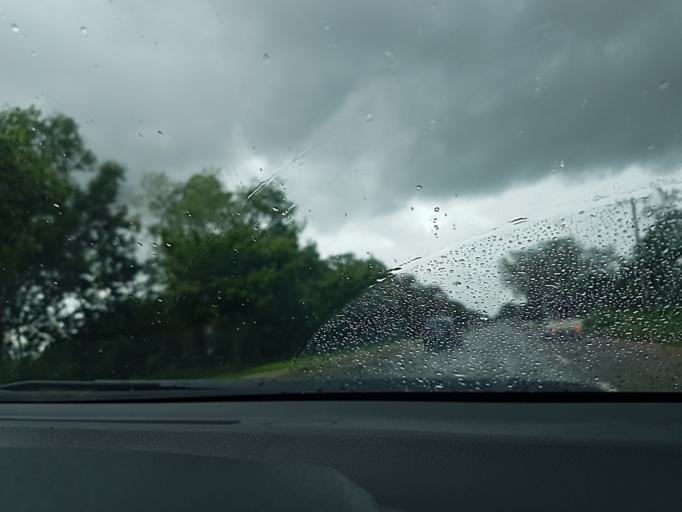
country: MM
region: Bago
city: Thanatpin
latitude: 17.1149
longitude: 96.2550
